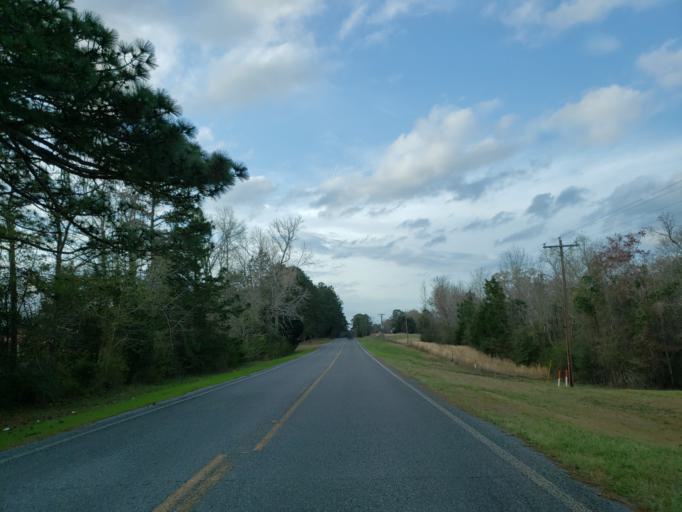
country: US
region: Mississippi
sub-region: Clarke County
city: Stonewall
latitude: 32.1867
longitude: -88.6786
